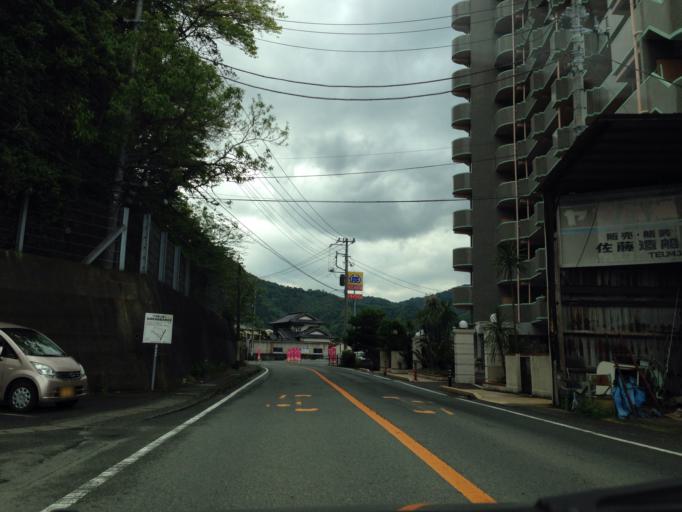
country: JP
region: Shizuoka
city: Numazu
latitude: 35.0289
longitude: 138.8934
